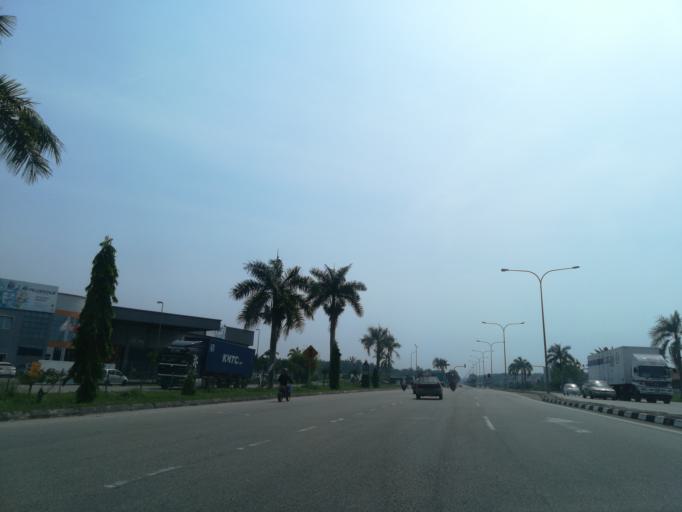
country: MY
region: Kedah
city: Kulim
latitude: 5.4330
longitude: 100.5510
